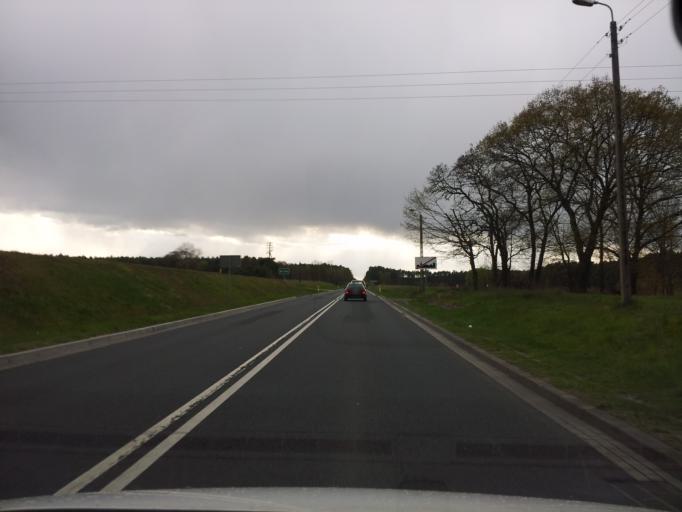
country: PL
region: Lubusz
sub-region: Powiat krosnienski
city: Bobrowice
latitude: 51.9951
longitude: 15.0148
